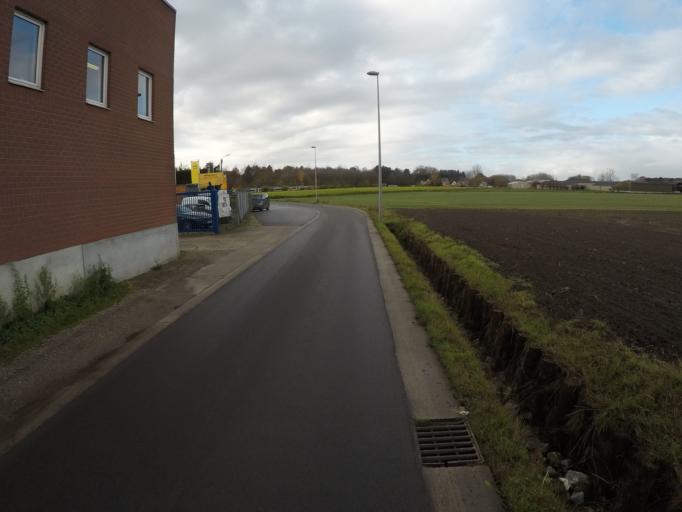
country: BE
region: Flanders
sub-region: Provincie Vlaams-Brabant
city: Londerzeel
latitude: 51.0117
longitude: 4.2937
